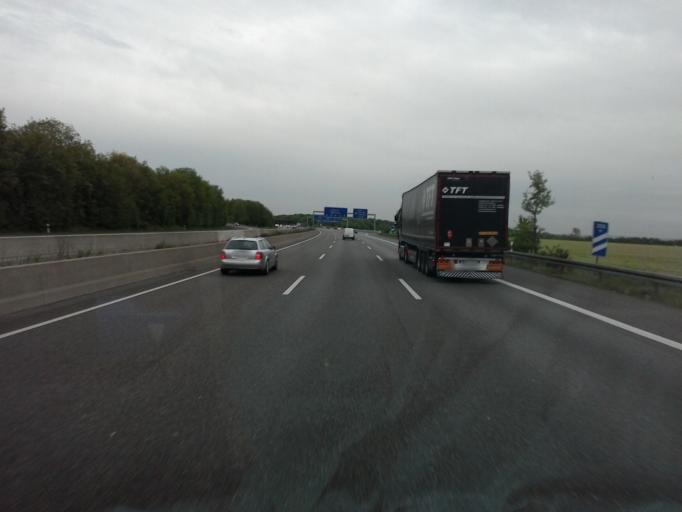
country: DE
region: North Rhine-Westphalia
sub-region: Regierungsbezirk Koln
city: Weilerswist
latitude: 50.7767
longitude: 6.8150
